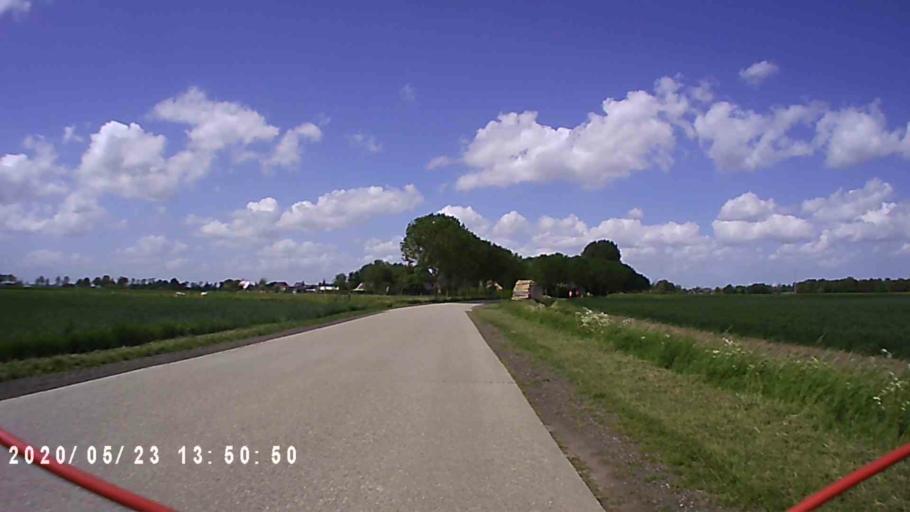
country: NL
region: Groningen
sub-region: Gemeente  Oldambt
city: Winschoten
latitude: 53.2667
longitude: 7.0401
